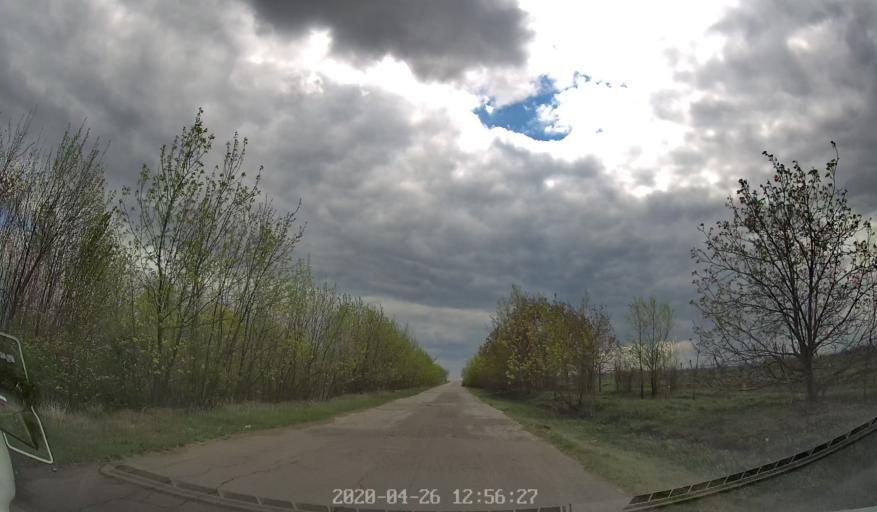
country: MD
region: Chisinau
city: Vadul lui Voda
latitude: 47.0728
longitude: 29.0663
